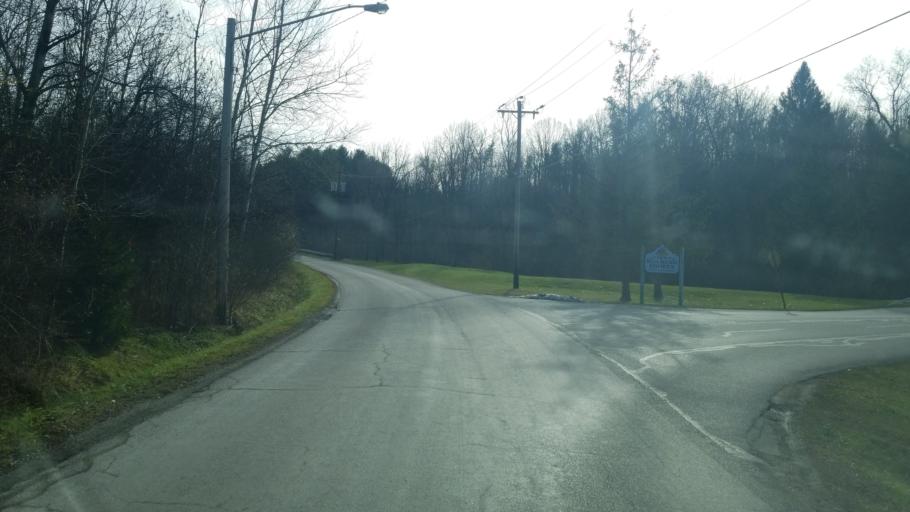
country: US
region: Ohio
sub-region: Ashtabula County
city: Roaming Shores
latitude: 41.6509
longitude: -80.8163
